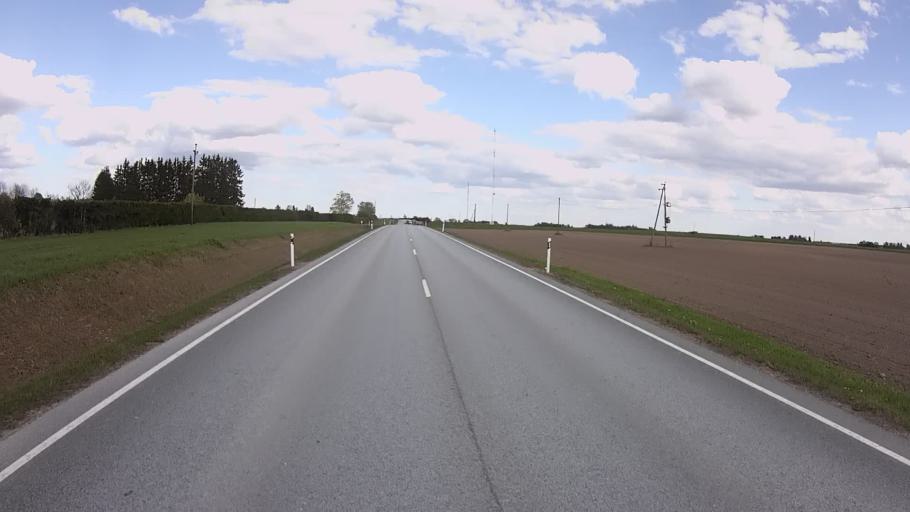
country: EE
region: Jogevamaa
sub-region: Jogeva linn
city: Jogeva
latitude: 58.8239
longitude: 26.6226
